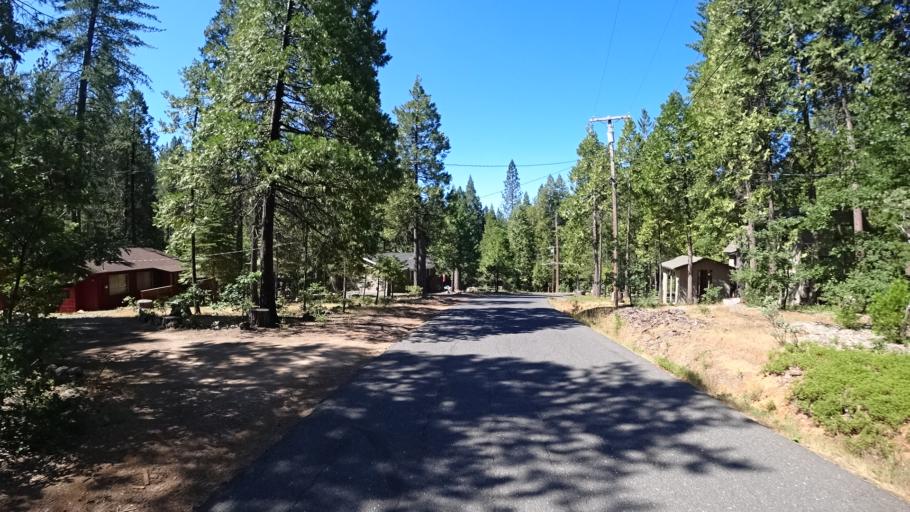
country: US
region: California
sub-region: Calaveras County
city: Arnold
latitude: 38.2422
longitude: -120.3752
